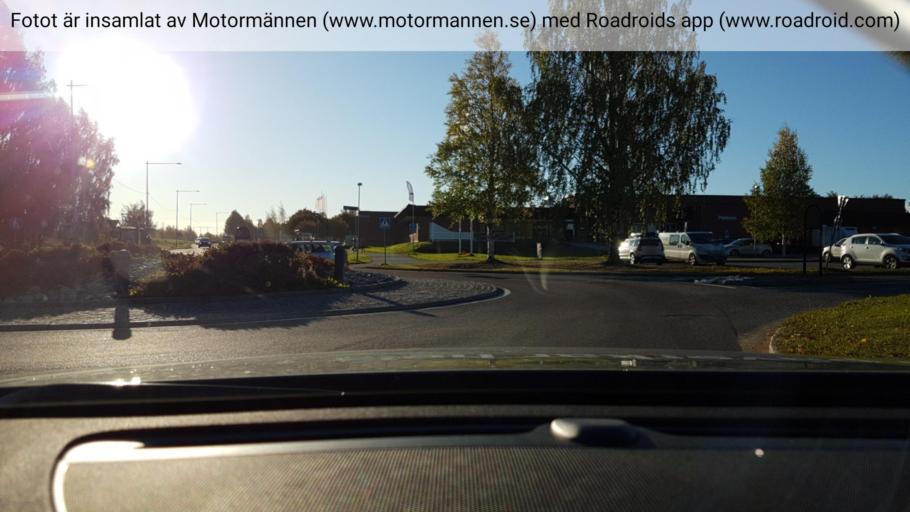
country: SE
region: Norrbotten
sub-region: Lulea Kommun
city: Gammelstad
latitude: 65.6423
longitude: 22.0128
